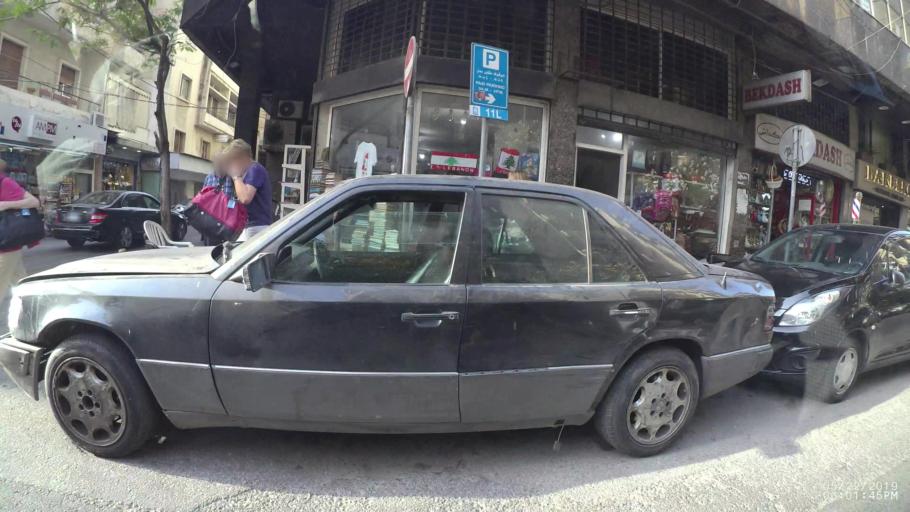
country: LB
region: Beyrouth
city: Ra's Bayrut
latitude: 33.8968
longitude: 35.4787
